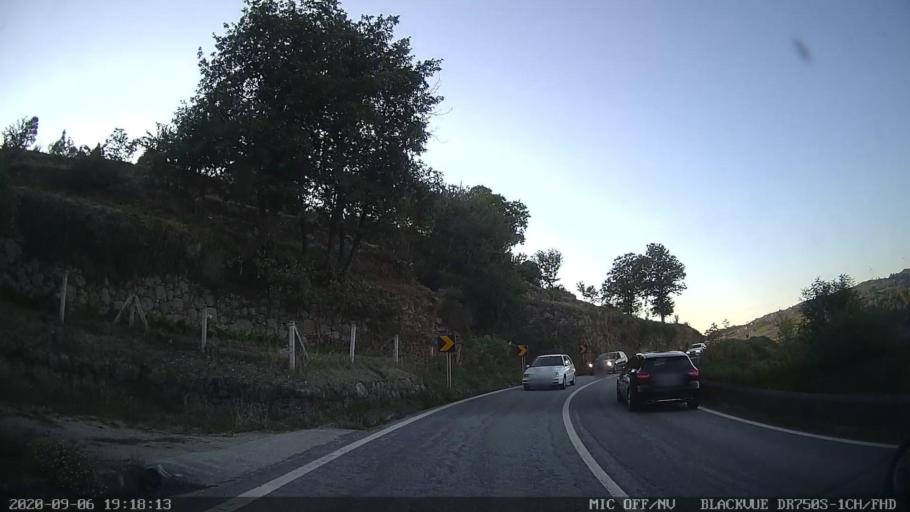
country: PT
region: Porto
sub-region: Baiao
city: Valadares
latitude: 41.1912
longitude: -7.9448
